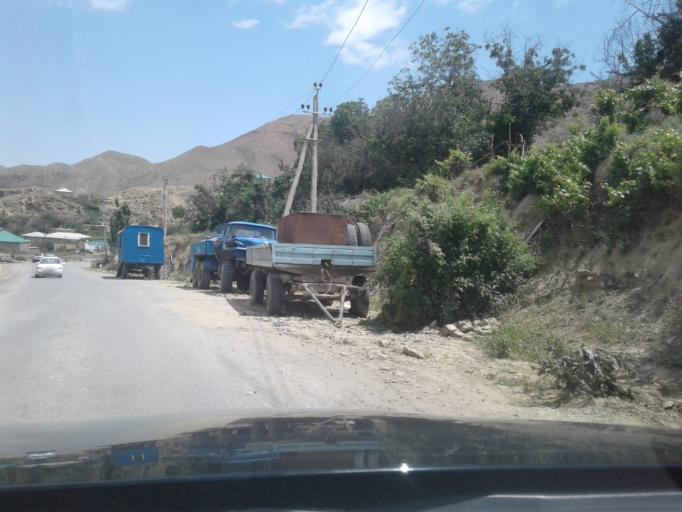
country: TM
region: Ahal
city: Baharly
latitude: 38.4674
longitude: 57.0344
